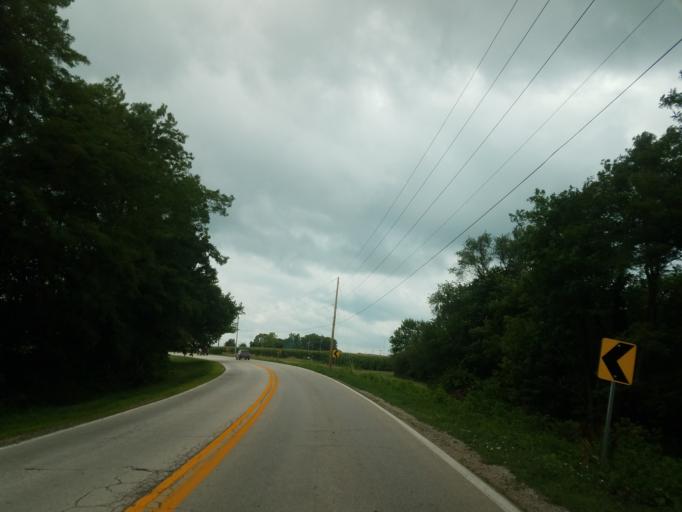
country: US
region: Illinois
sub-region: McLean County
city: Bloomington
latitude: 40.4837
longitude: -89.0314
